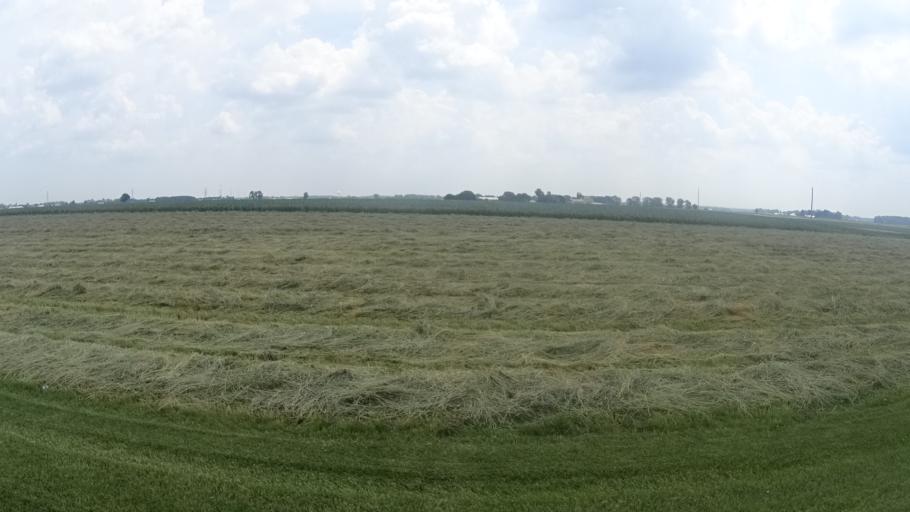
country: US
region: Ohio
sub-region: Erie County
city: Milan
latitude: 41.3237
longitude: -82.6735
